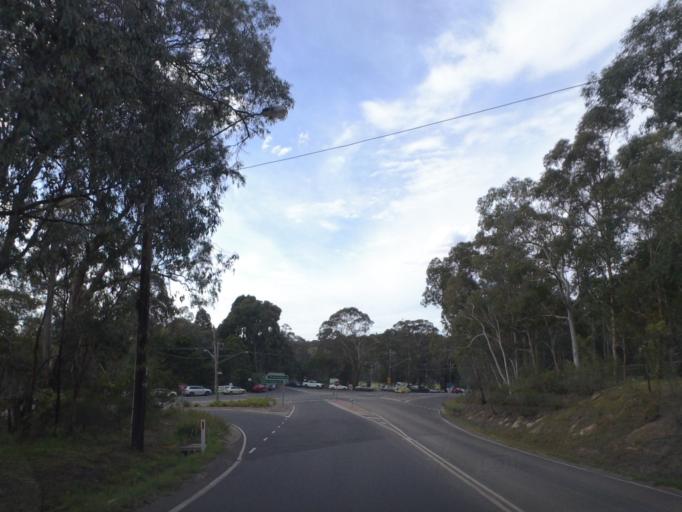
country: AU
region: Victoria
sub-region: Nillumbik
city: Eltham
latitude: -37.7531
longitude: 145.1742
